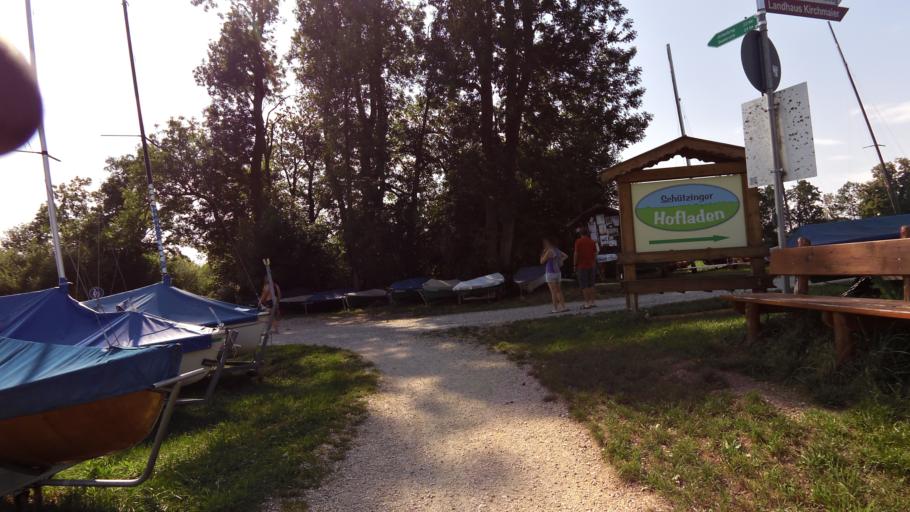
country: DE
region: Bavaria
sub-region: Upper Bavaria
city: Chieming
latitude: 47.9055
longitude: 12.5085
